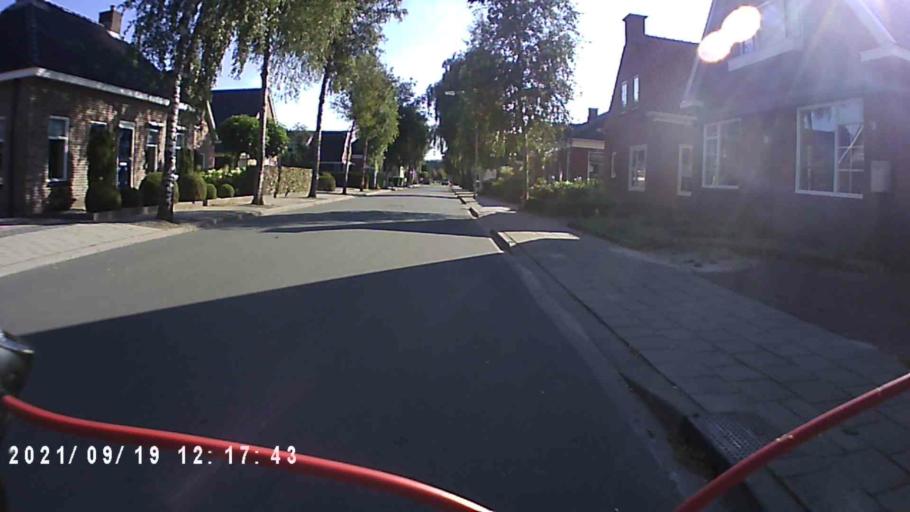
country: NL
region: Groningen
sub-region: Gemeente Slochteren
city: Slochteren
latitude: 53.2495
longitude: 6.8678
